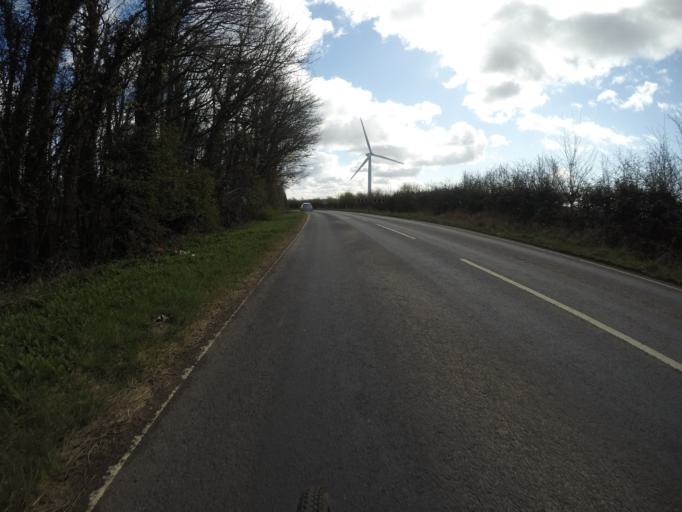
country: GB
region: Scotland
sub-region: North Ayrshire
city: Dreghorn
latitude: 55.5948
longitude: -4.6223
